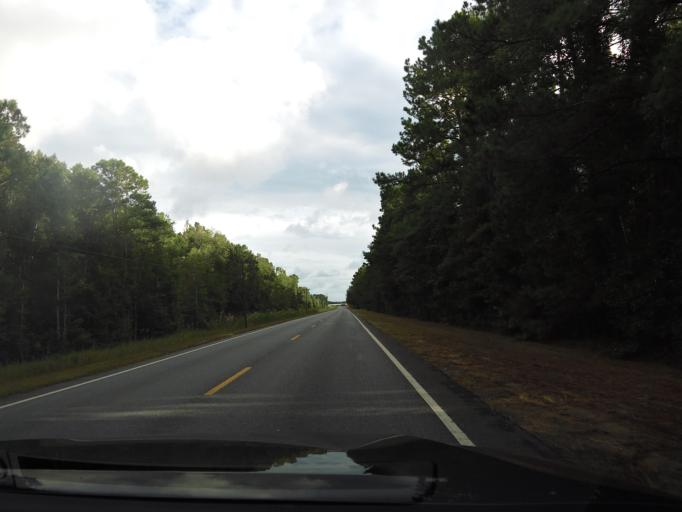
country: US
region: Georgia
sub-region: Liberty County
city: Midway
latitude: 31.6642
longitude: -81.3989
